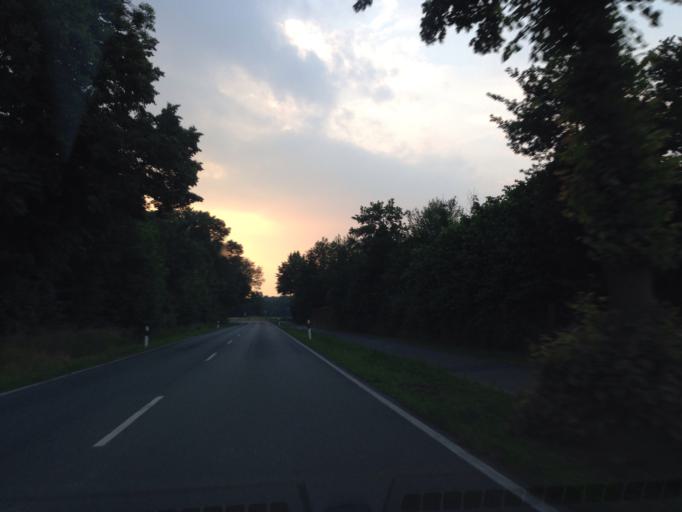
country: DE
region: North Rhine-Westphalia
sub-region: Regierungsbezirk Munster
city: Altenberge
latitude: 51.9667
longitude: 7.5116
